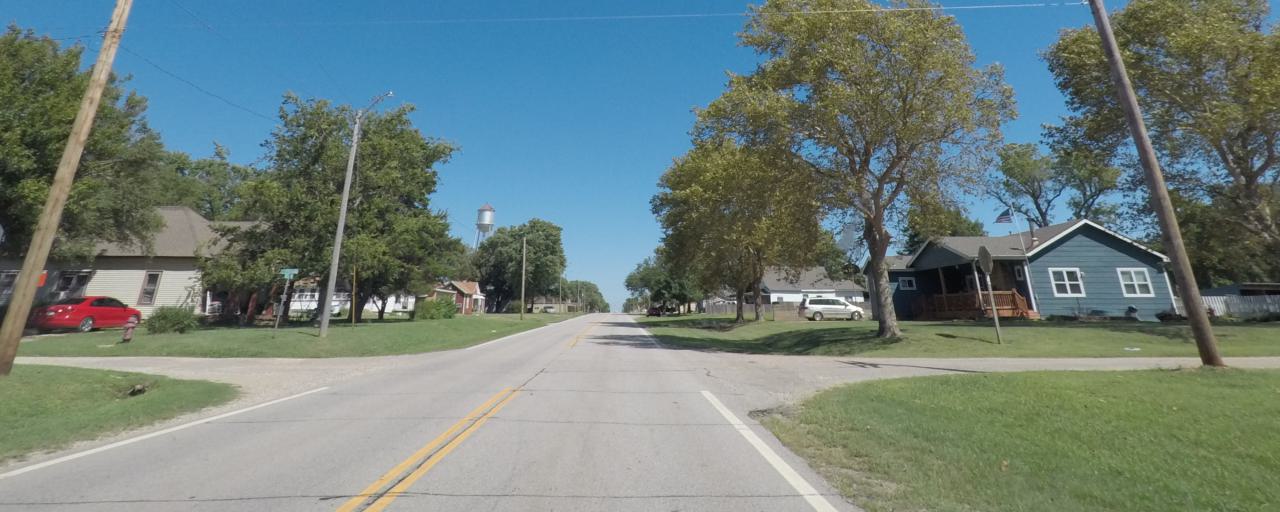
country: US
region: Kansas
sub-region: Sumner County
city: Caldwell
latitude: 37.0459
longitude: -97.4011
